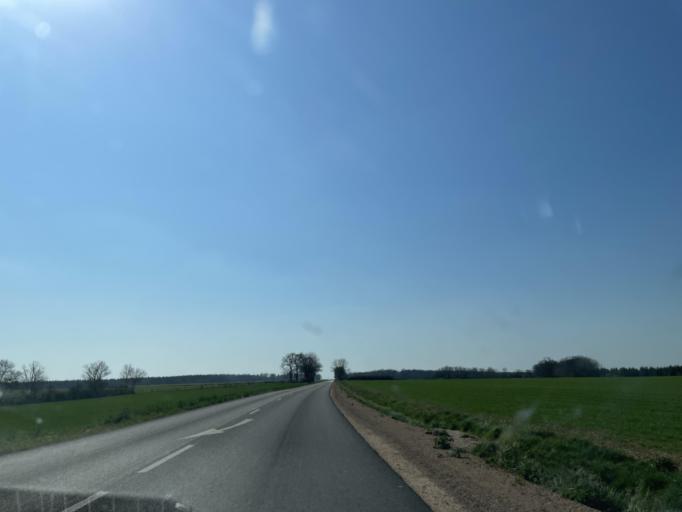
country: FR
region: Bourgogne
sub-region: Departement de la Cote-d'Or
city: Semur-en-Auxois
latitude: 47.4567
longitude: 4.3405
